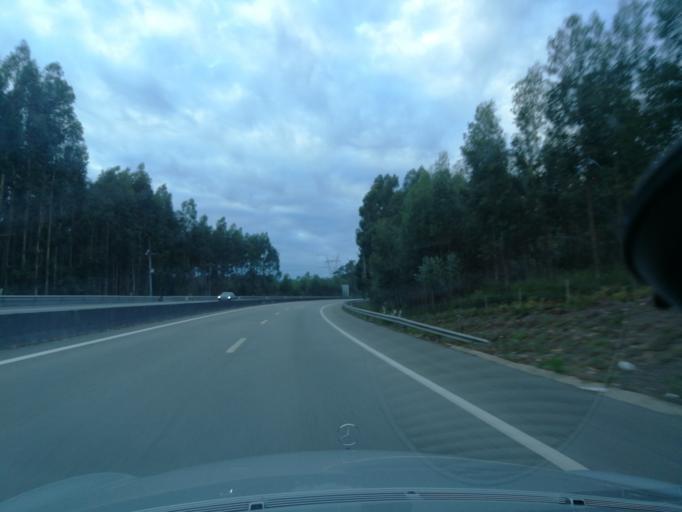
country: PT
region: Aveiro
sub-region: Albergaria-A-Velha
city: Albergaria-a-Velha
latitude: 40.6817
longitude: -8.4949
